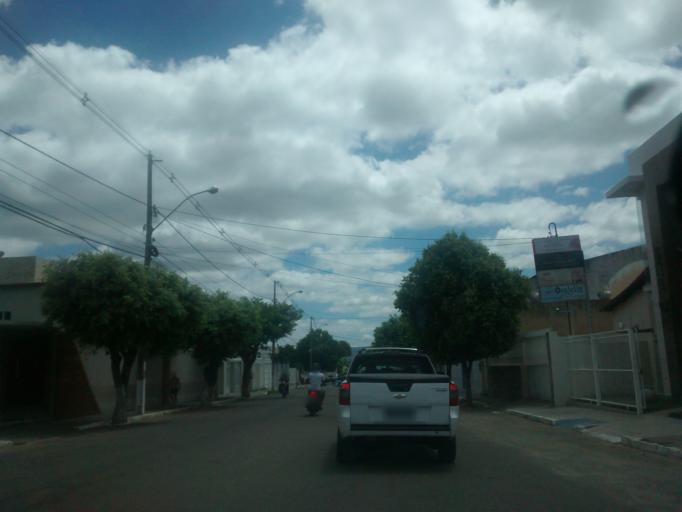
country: BR
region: Bahia
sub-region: Brumado
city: Brumado
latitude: -14.2057
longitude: -41.6731
